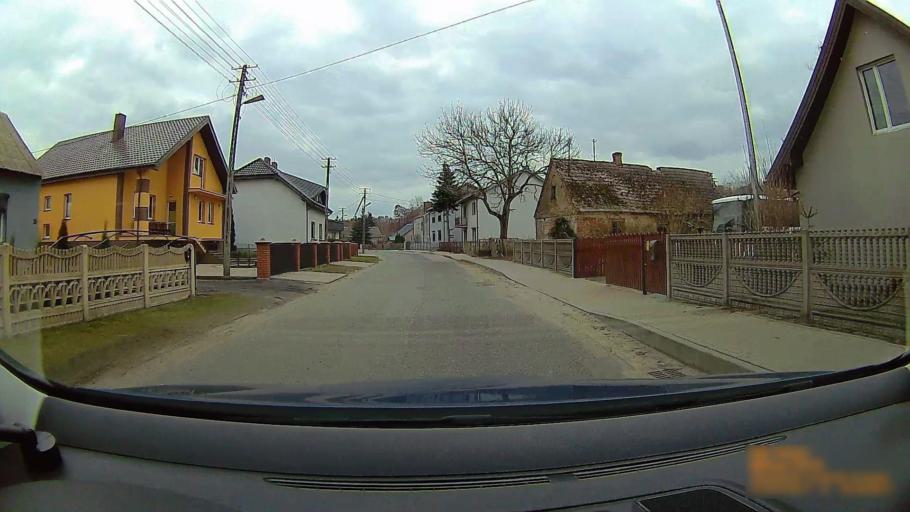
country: PL
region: Greater Poland Voivodeship
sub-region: Powiat koninski
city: Rzgow Pierwszy
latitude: 52.1301
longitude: 18.0610
